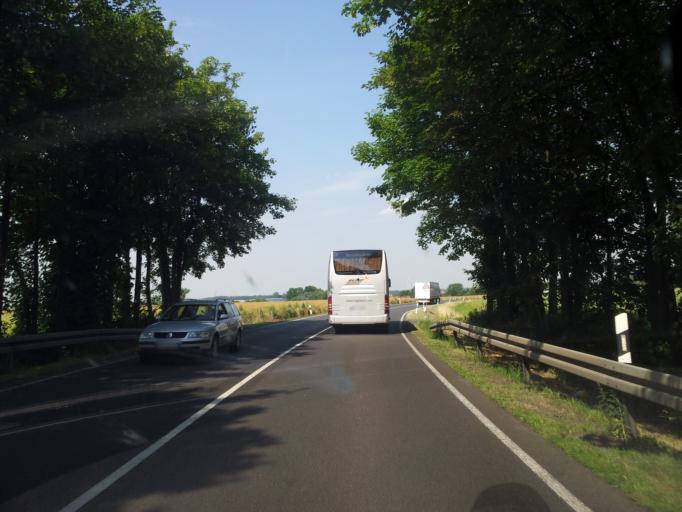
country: DE
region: Saxony
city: Ostrau
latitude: 51.2315
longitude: 13.1608
